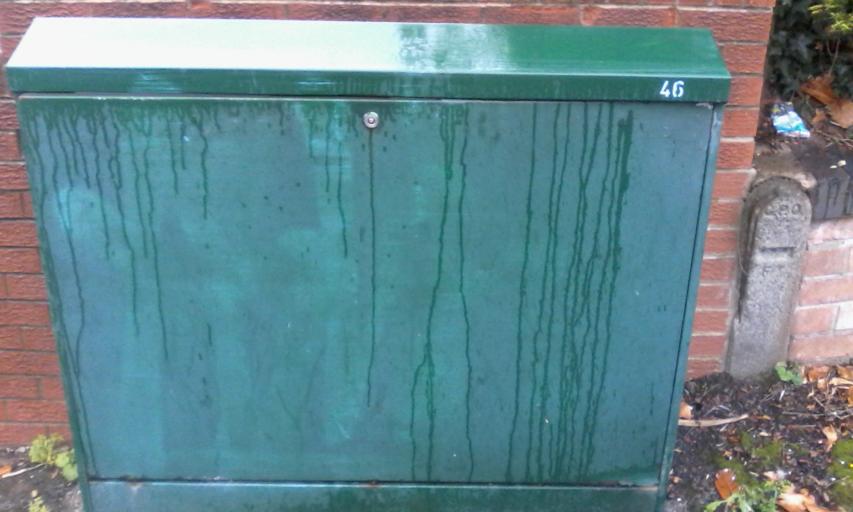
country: GB
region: England
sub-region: Nottinghamshire
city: Arnold
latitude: 52.9786
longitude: -1.1036
